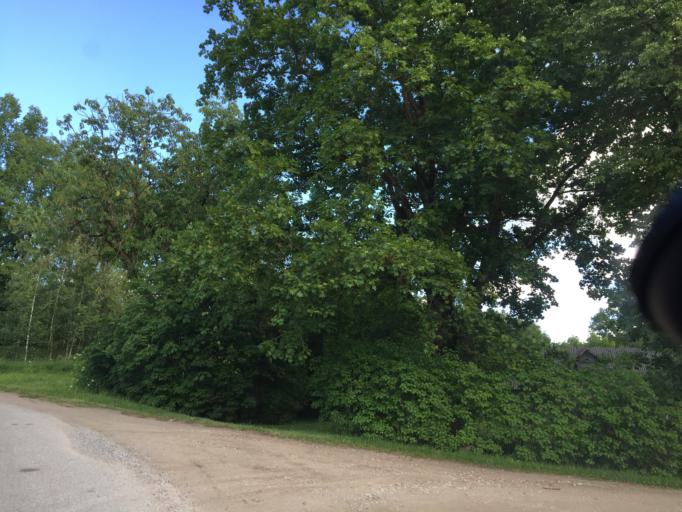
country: LT
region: Panevezys
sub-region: Birzai
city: Birzai
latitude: 56.3796
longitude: 24.6512
